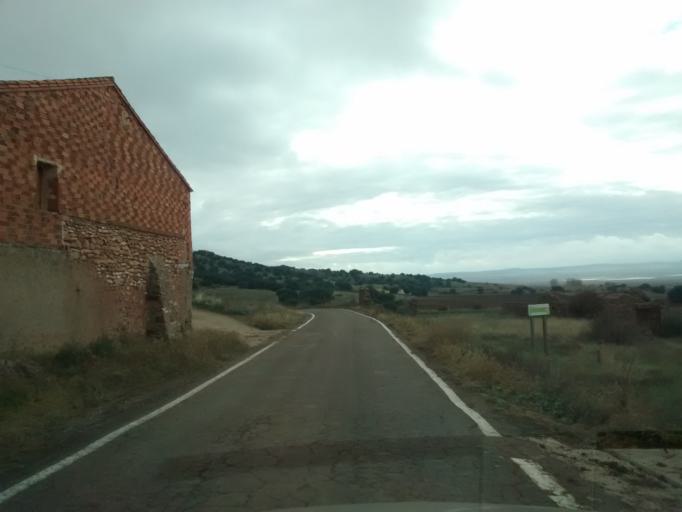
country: ES
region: Aragon
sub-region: Provincia de Zaragoza
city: Gallocanta
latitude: 40.9897
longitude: -1.4680
